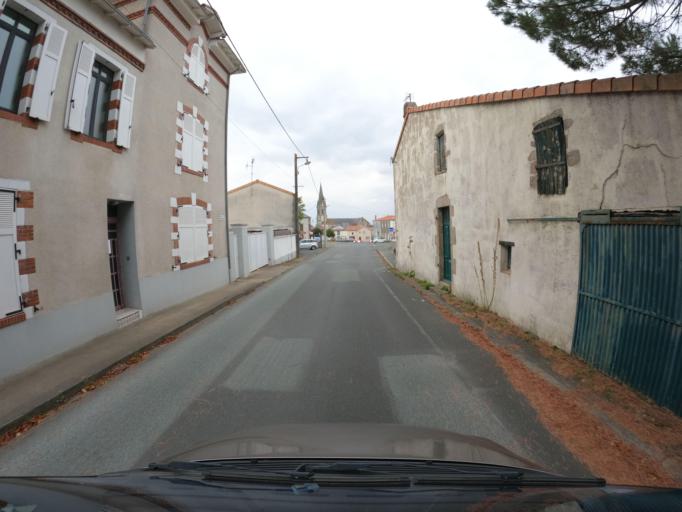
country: FR
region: Pays de la Loire
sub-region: Departement de la Vendee
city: Tiffauges
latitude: 47.0122
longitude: -1.1111
